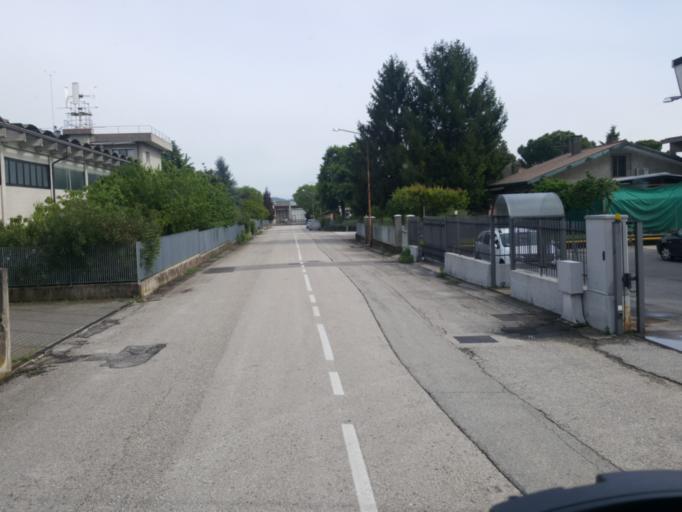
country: IT
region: Veneto
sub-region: Provincia di Vicenza
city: Montecchio Maggiore-Alte Ceccato
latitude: 45.4940
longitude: 11.4033
